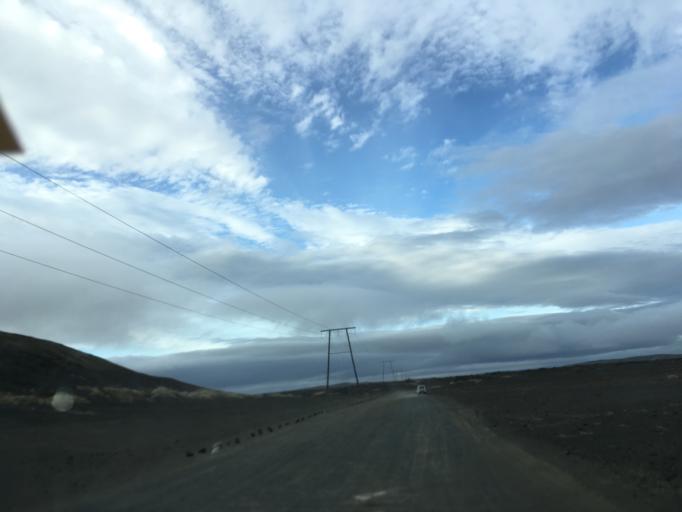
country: IS
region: South
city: Vestmannaeyjar
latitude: 64.1273
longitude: -19.1204
